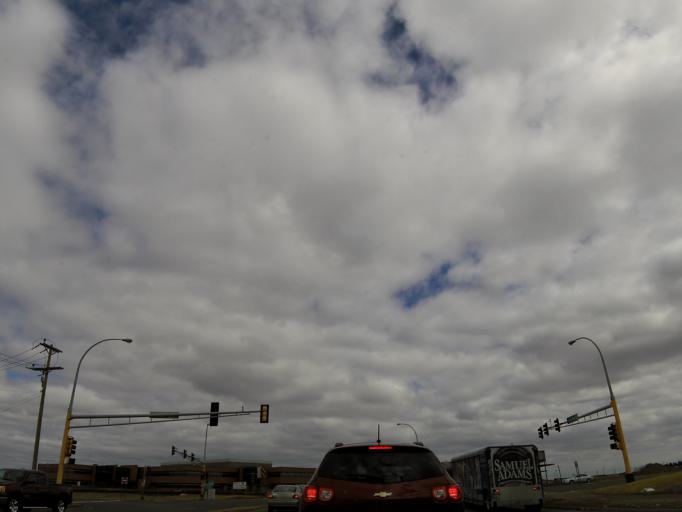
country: US
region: Minnesota
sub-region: Washington County
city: Woodbury
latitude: 44.9439
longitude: -92.9351
